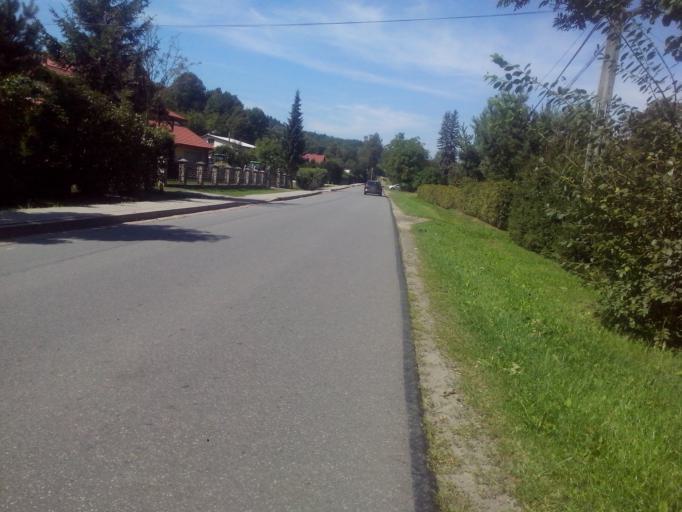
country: PL
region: Subcarpathian Voivodeship
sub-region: Powiat strzyzowski
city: Frysztak
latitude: 49.8652
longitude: 21.6195
